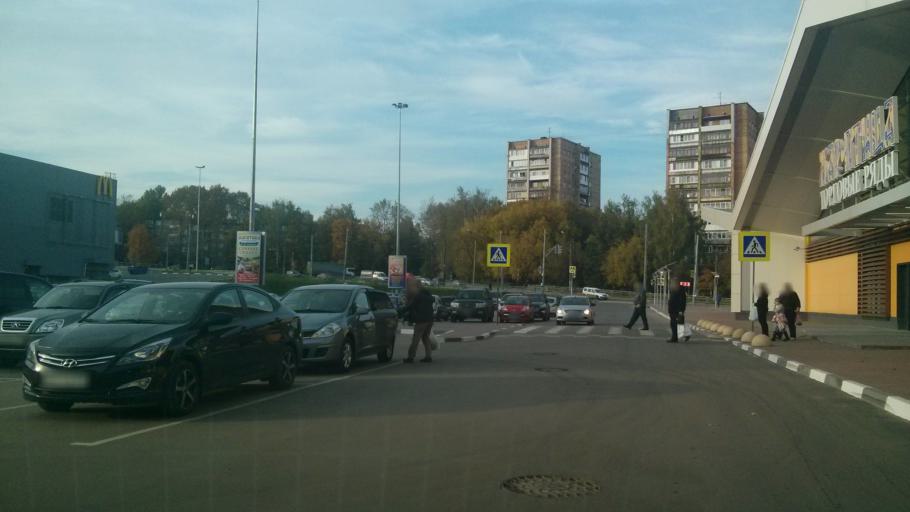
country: RU
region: Nizjnij Novgorod
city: Nizhniy Novgorod
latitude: 56.2956
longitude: 44.0452
